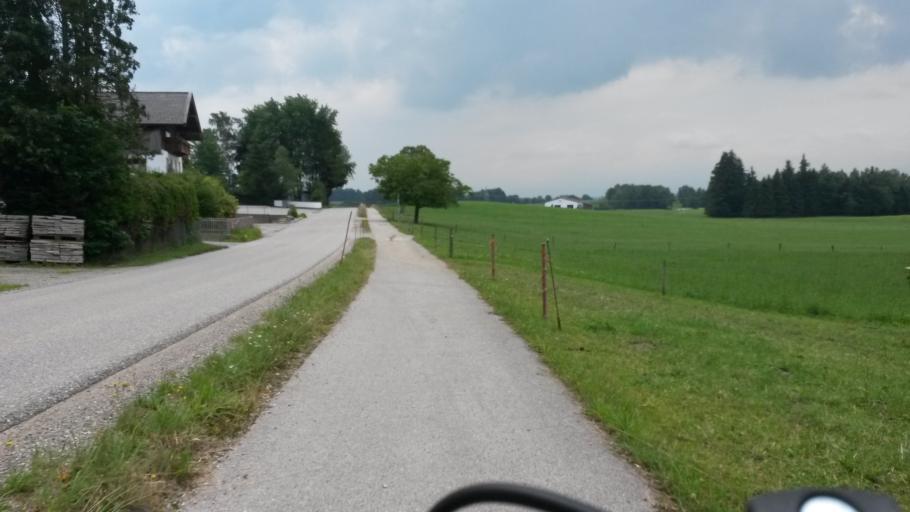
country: DE
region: Bavaria
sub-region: Upper Bavaria
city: Hoslwang
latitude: 47.9649
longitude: 12.3208
